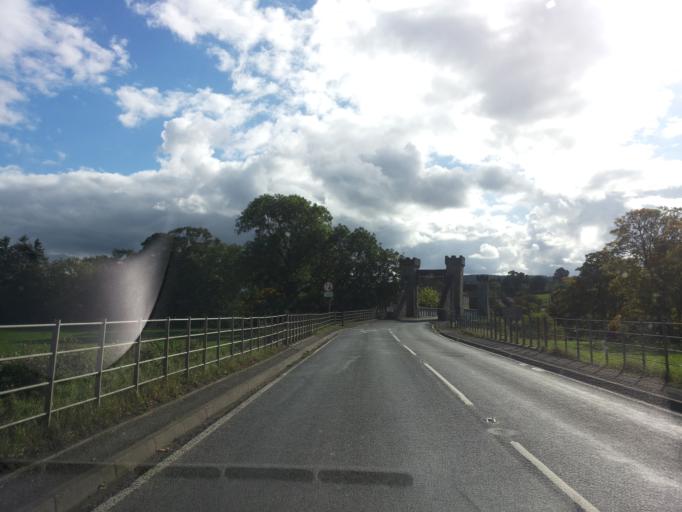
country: GB
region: England
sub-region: North Yorkshire
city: Leyburn
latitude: 54.2951
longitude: -1.8192
